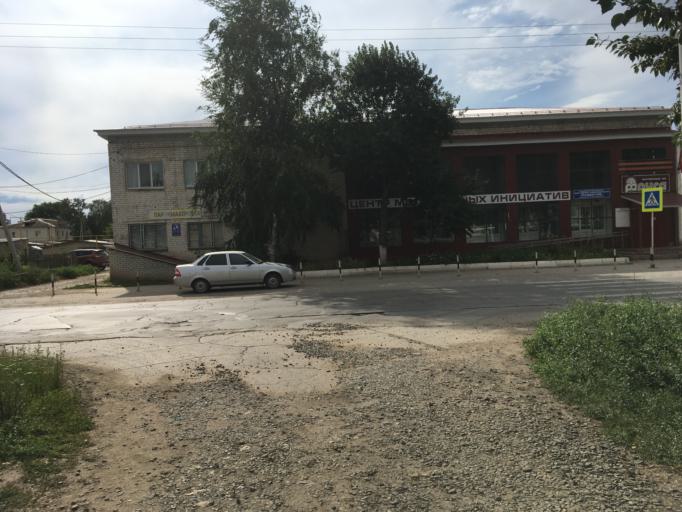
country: RU
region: Samara
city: Bezenchuk
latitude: 52.9875
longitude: 49.4410
